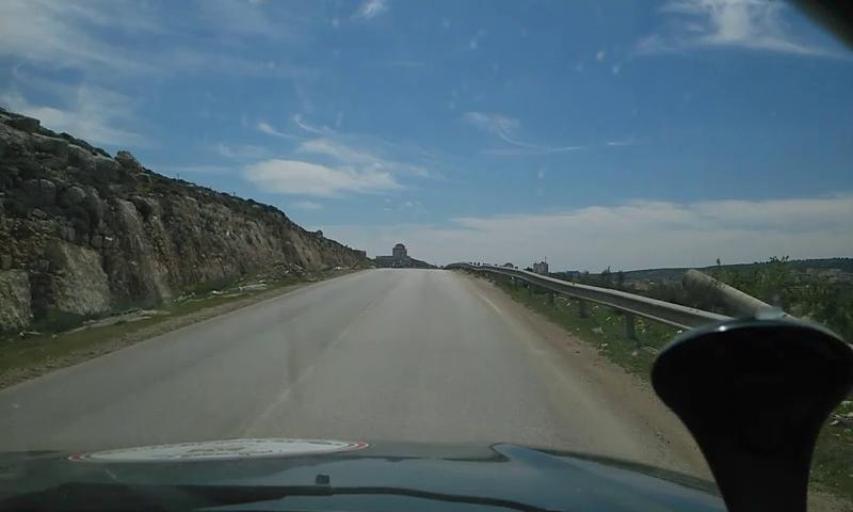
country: PS
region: West Bank
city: Al Judayrah
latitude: 31.8576
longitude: 35.2016
